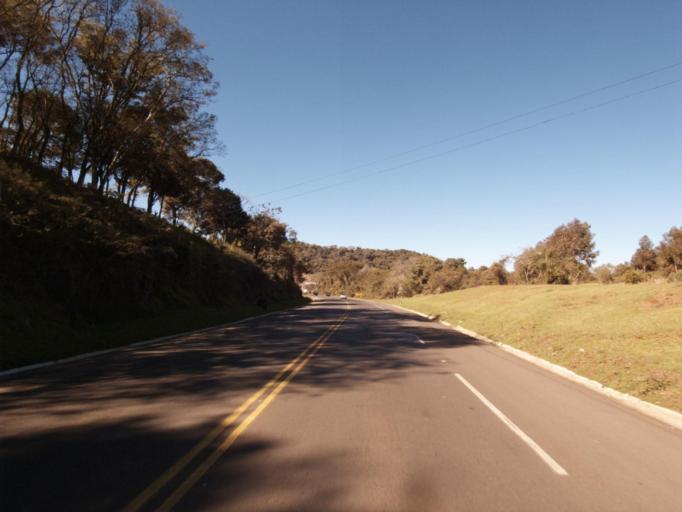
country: BR
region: Santa Catarina
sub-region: Chapeco
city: Chapeco
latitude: -26.9965
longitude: -52.6362
